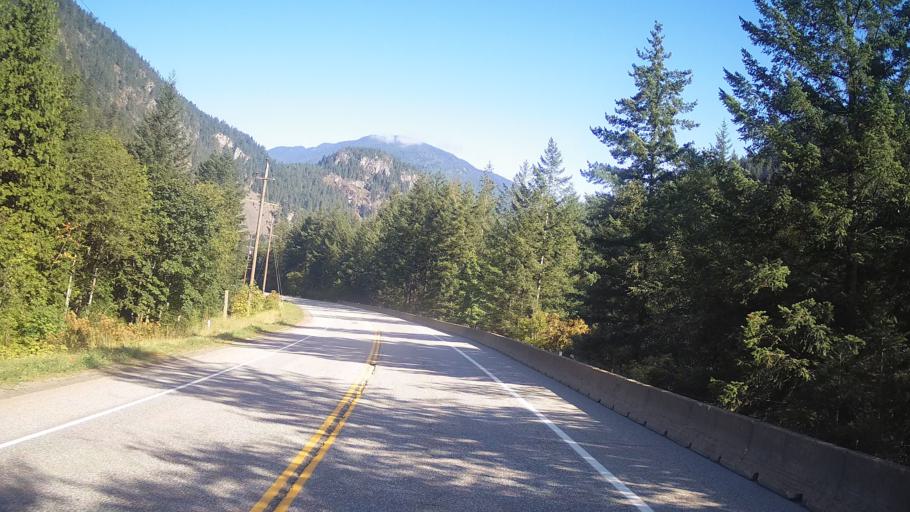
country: CA
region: British Columbia
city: Hope
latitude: 49.6320
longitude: -121.3941
